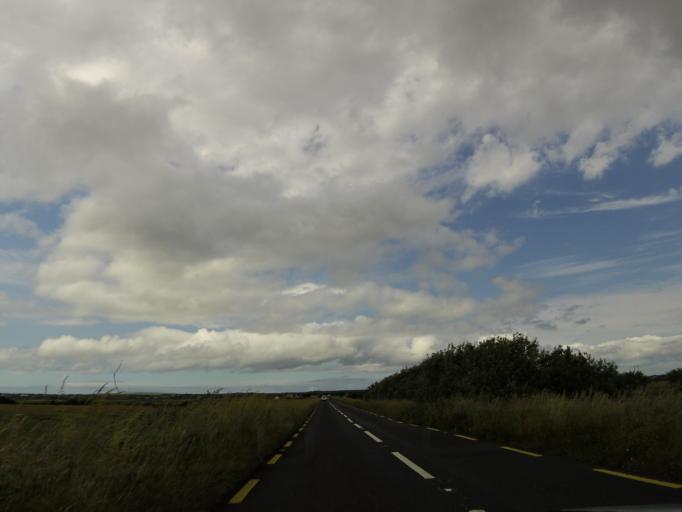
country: IE
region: Munster
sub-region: An Clar
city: Kilrush
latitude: 52.6608
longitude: -9.5301
